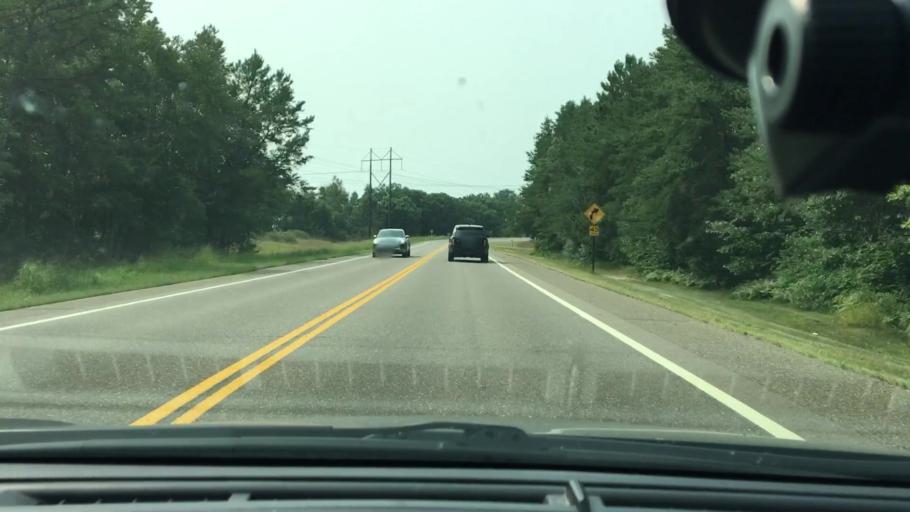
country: US
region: Minnesota
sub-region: Cass County
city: East Gull Lake
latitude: 46.3806
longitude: -94.3329
